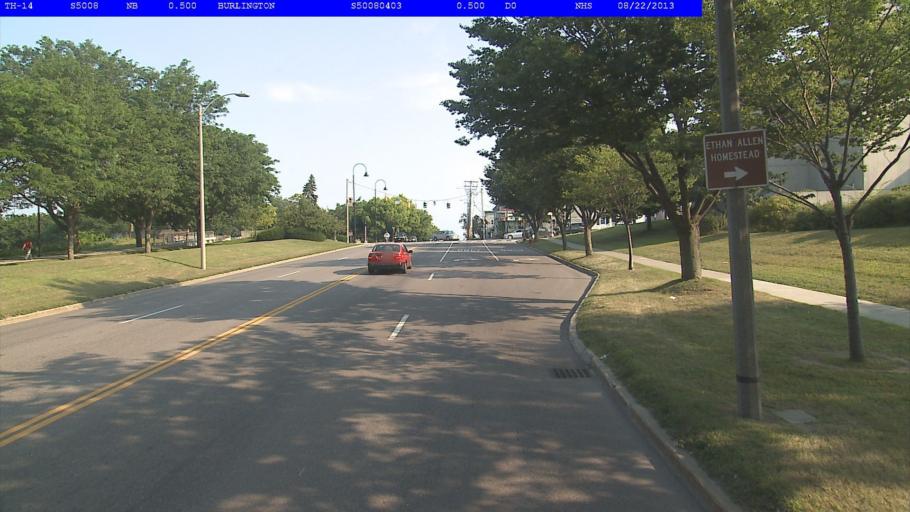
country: US
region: Vermont
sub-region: Chittenden County
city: Burlington
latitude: 44.4796
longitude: -73.2189
